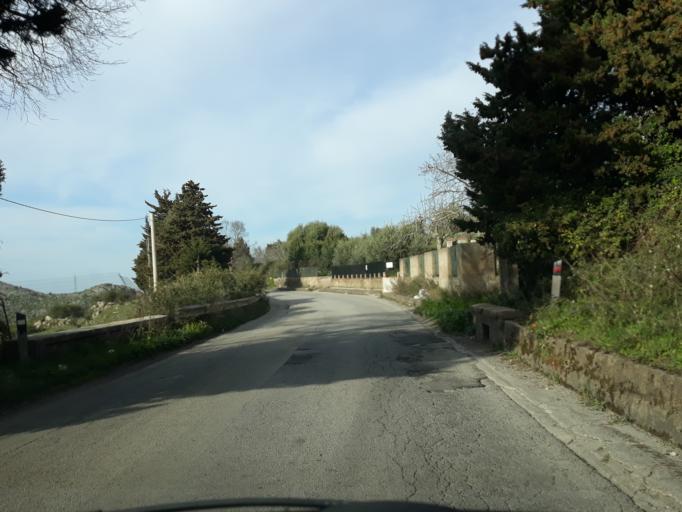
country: IT
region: Sicily
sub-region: Palermo
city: Torretta
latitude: 38.1048
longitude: 13.2337
